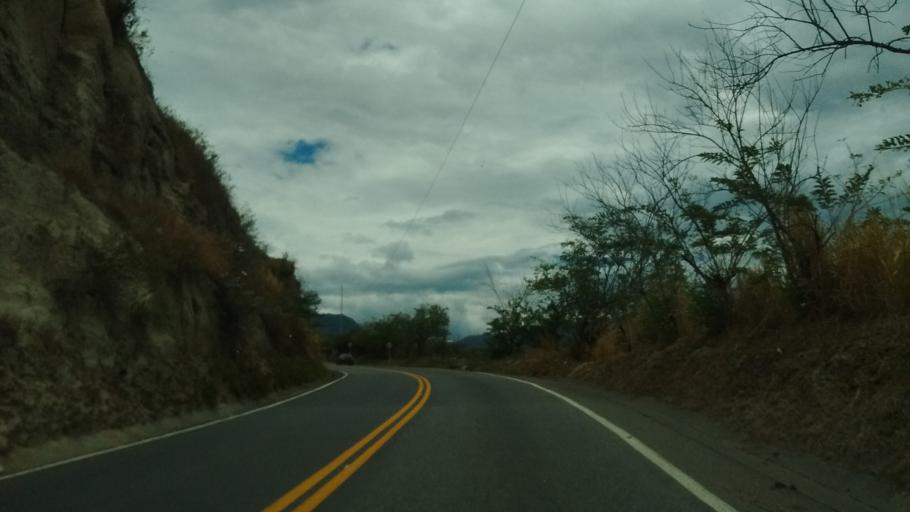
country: CO
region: Cauca
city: La Sierra
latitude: 2.2225
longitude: -76.7962
